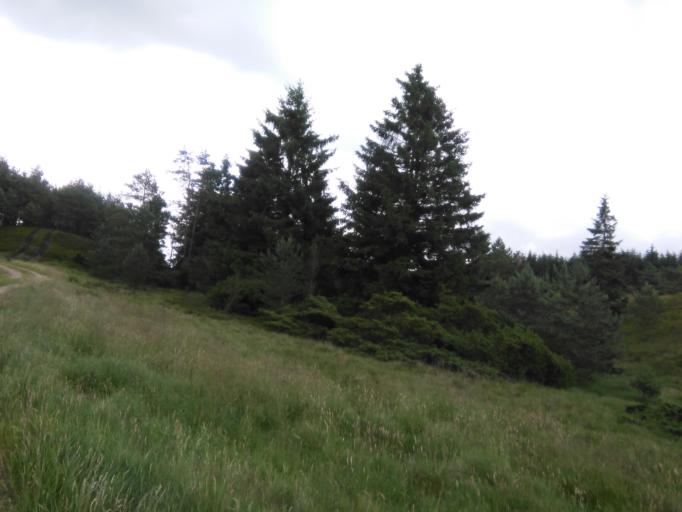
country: DK
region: Central Jutland
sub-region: Silkeborg Kommune
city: Virklund
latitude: 56.0776
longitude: 9.4563
